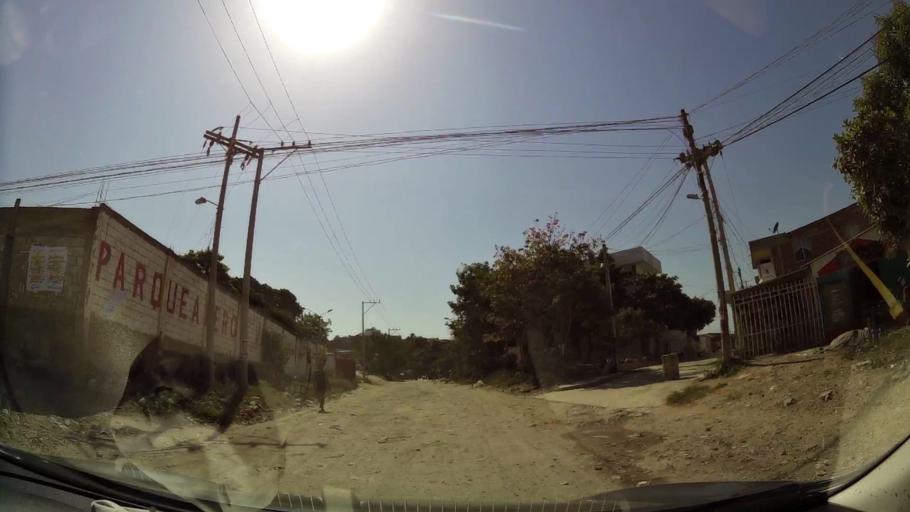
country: CO
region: Bolivar
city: Cartagena
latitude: 10.3743
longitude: -75.4965
